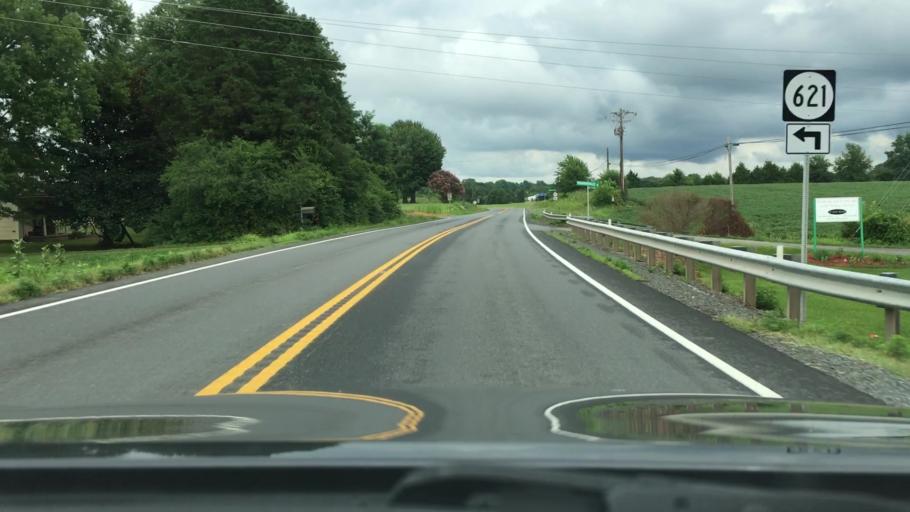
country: US
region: Virginia
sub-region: Orange County
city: Orange
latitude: 38.2720
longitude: -77.9040
